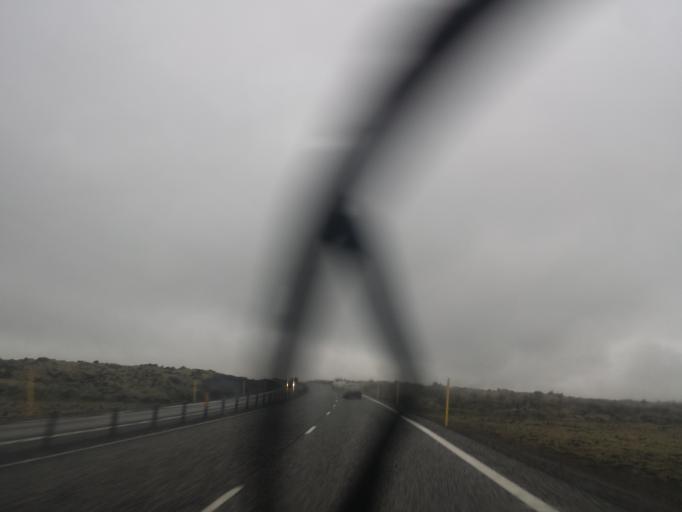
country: IS
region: South
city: THorlakshoefn
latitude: 64.0313
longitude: -21.4296
